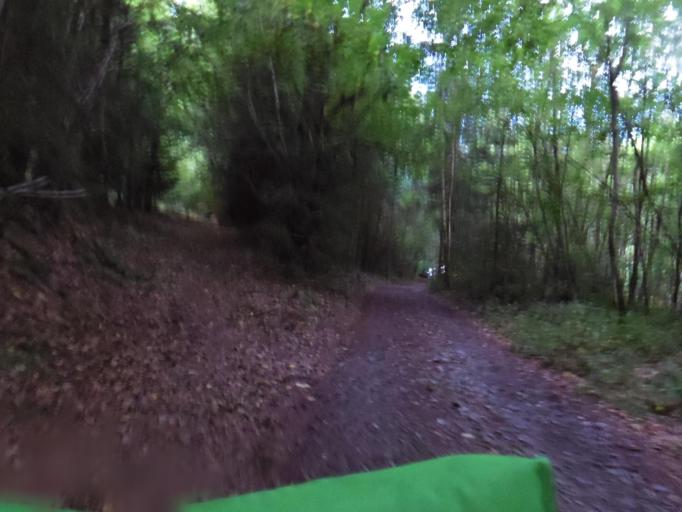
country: BE
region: Wallonia
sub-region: Province de Namur
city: Bievre
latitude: 49.8670
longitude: 4.9913
